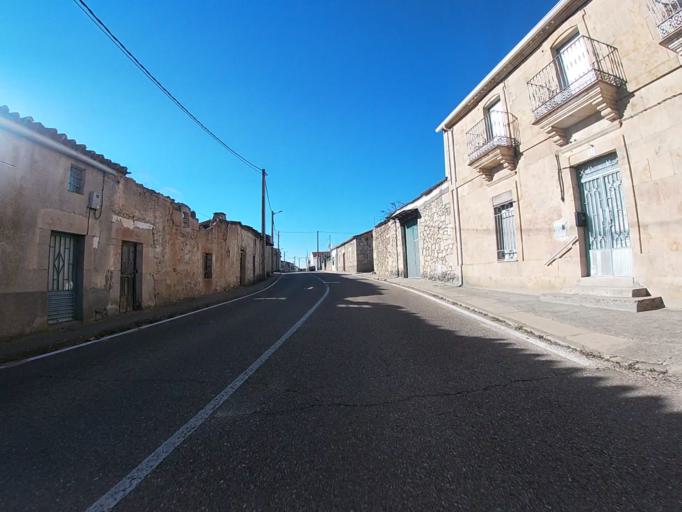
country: ES
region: Castille and Leon
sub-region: Provincia de Salamanca
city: Almenara de Tormes
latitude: 41.0639
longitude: -5.8213
